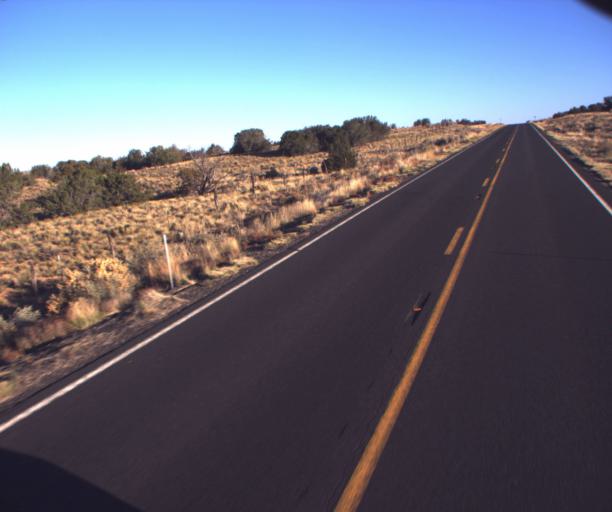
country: US
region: Arizona
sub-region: Apache County
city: Houck
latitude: 35.2259
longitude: -109.4397
